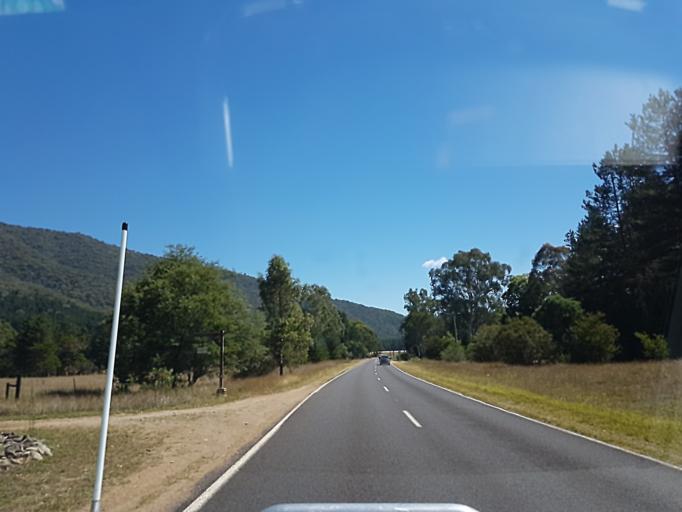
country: AU
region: Victoria
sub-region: Alpine
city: Mount Beauty
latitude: -36.7654
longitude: 147.0245
